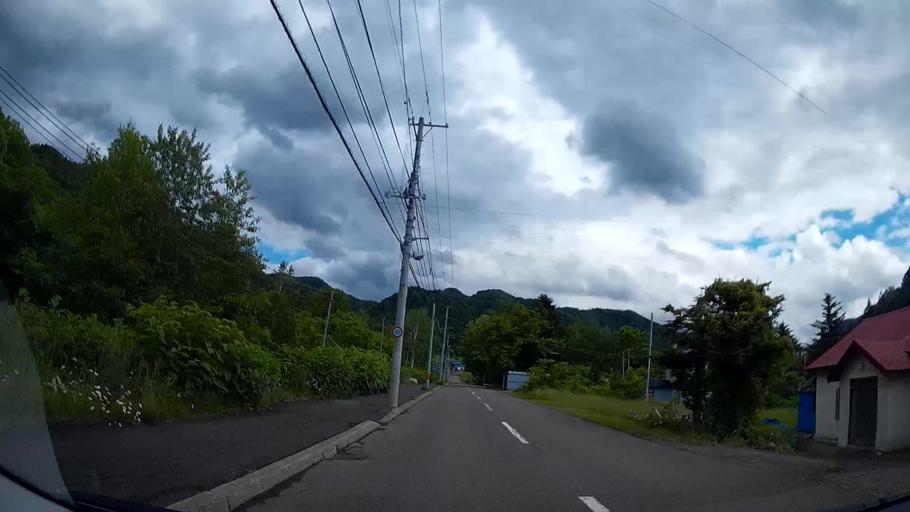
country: JP
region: Hokkaido
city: Sapporo
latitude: 42.9508
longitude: 141.1528
